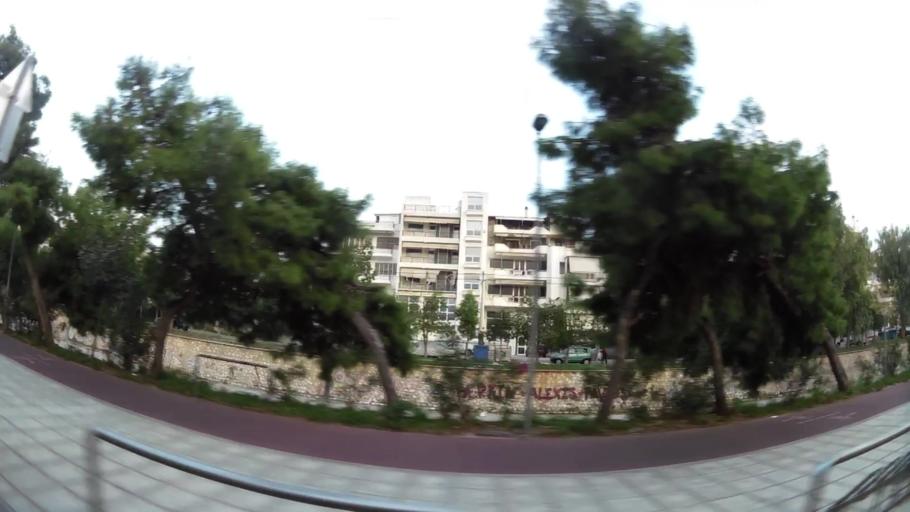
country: GR
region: Attica
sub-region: Nomarchia Athinas
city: Moskhaton
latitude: 37.9514
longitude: 23.6870
